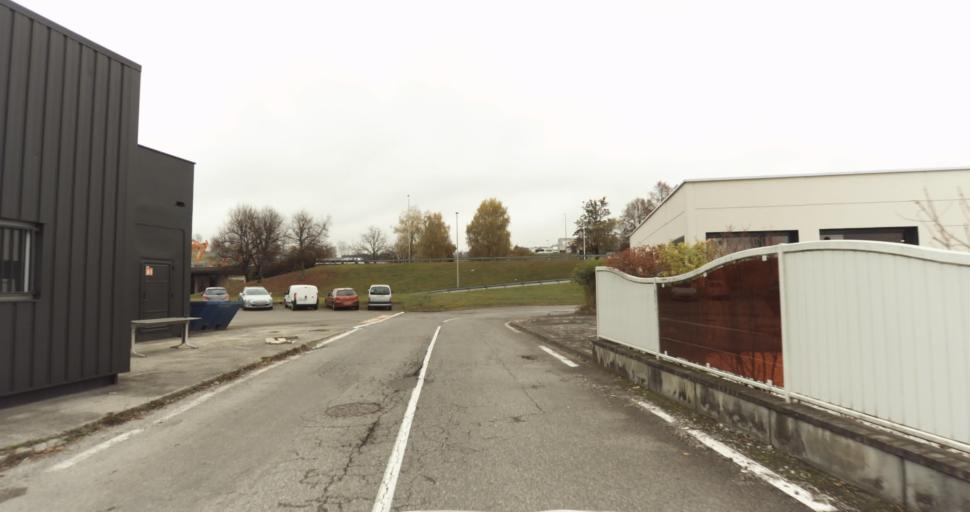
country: FR
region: Rhone-Alpes
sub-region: Departement de la Haute-Savoie
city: Alby-sur-Cheran
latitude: 45.8186
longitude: 6.0008
